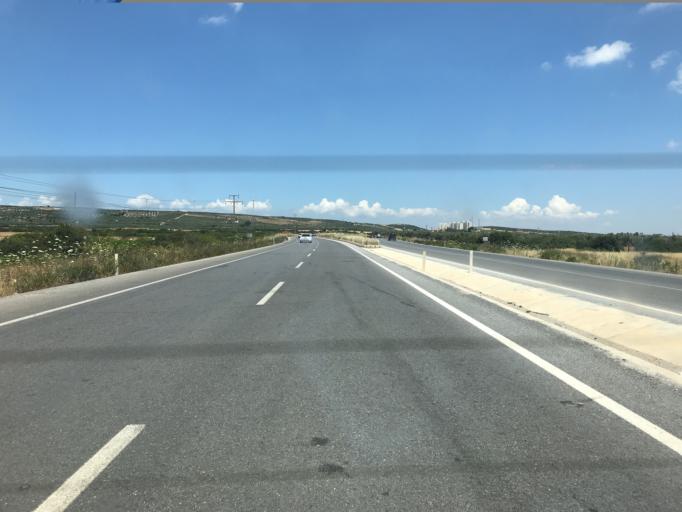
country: TR
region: Aydin
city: Akkoy
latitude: 37.4605
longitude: 27.3397
